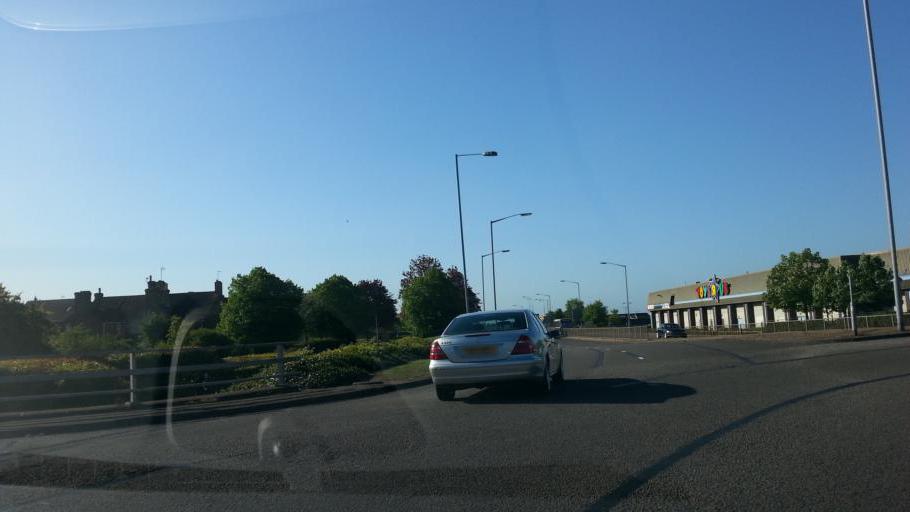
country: GB
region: England
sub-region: Peterborough
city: Peterborough
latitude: 52.5837
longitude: -0.2525
